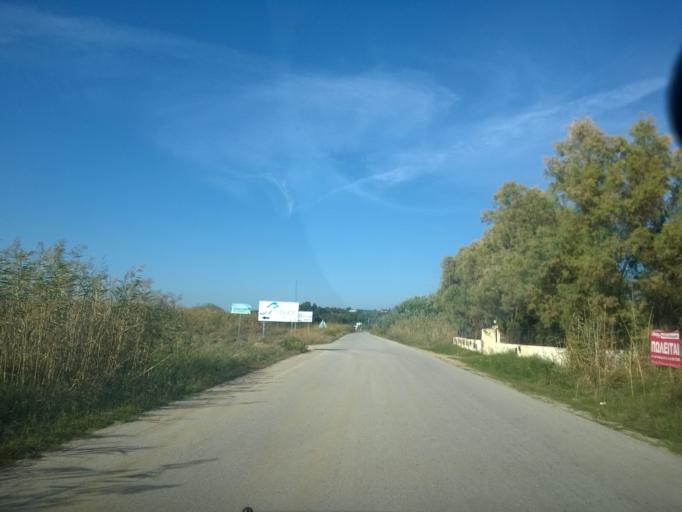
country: GR
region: Central Macedonia
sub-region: Nomos Chalkidikis
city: Nea Kallikrateia
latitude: 40.3277
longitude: 23.0231
